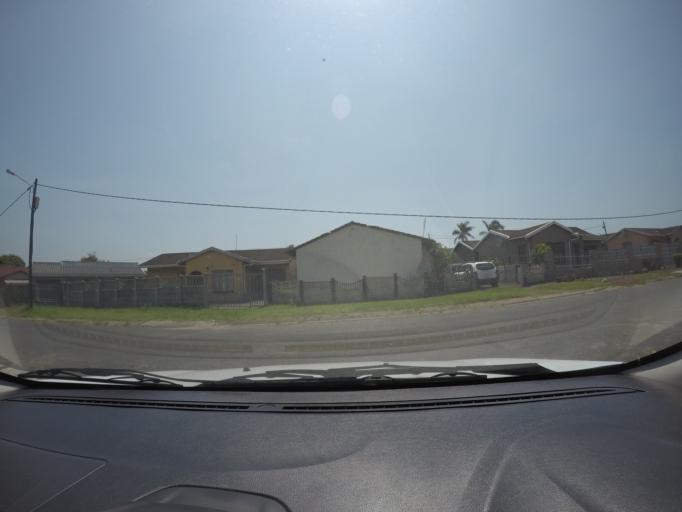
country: ZA
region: KwaZulu-Natal
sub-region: uThungulu District Municipality
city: eSikhawini
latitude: -28.8638
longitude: 31.9233
